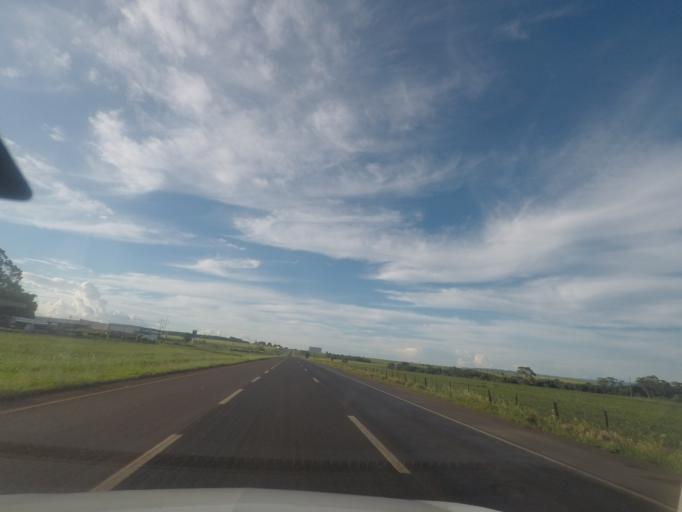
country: BR
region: Goias
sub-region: Itumbiara
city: Itumbiara
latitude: -18.3249
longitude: -49.2273
